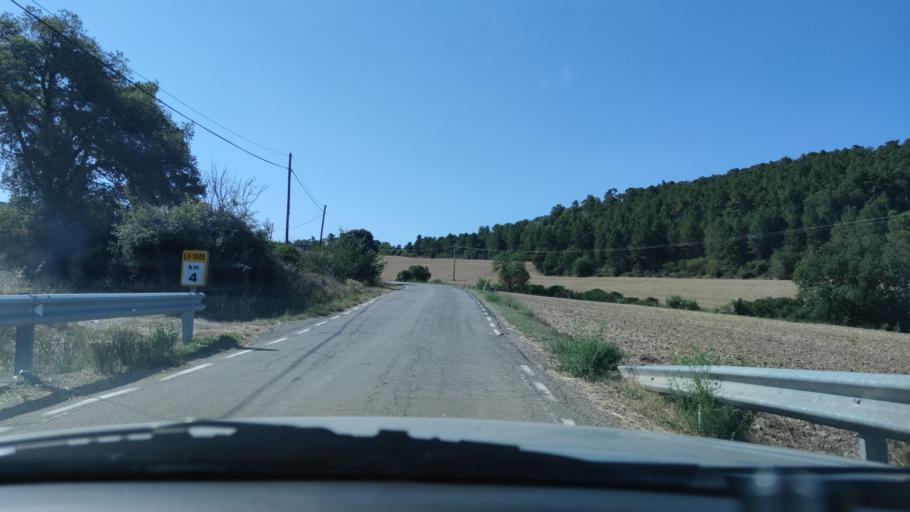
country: ES
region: Catalonia
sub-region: Provincia de Lleida
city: Sant Guim de Freixenet
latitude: 41.6856
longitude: 1.3959
